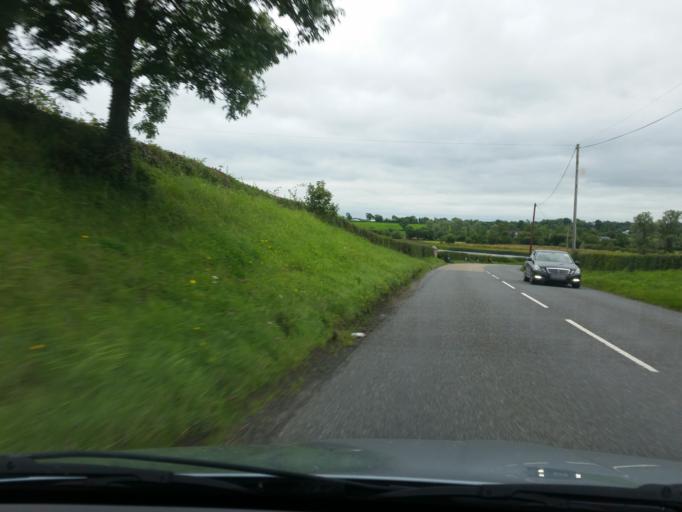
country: GB
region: Northern Ireland
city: Lisnaskea
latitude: 54.1952
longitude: -7.5090
